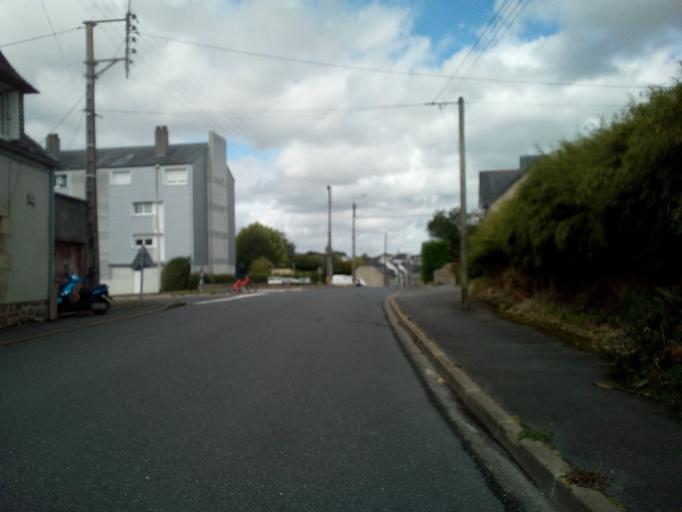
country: FR
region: Brittany
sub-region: Departement du Finistere
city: Landivisiau
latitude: 48.5056
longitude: -4.0755
